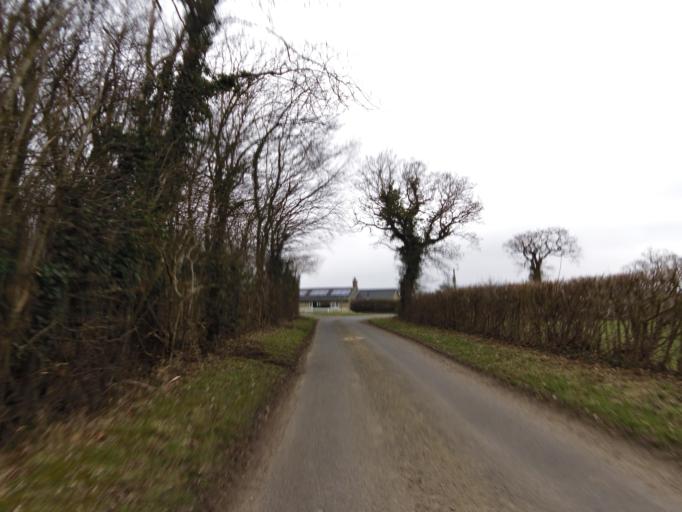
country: GB
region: England
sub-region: Suffolk
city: Cookley
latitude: 52.2577
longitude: 1.4196
